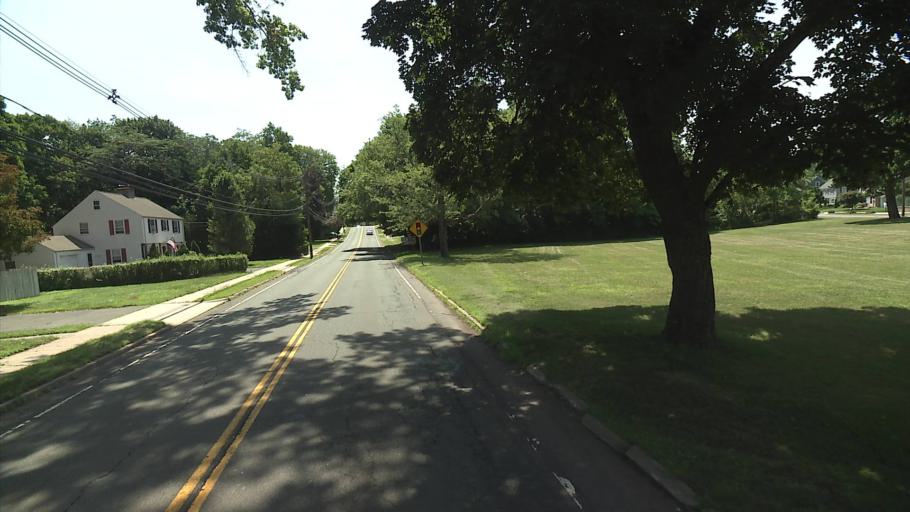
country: US
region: Connecticut
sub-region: Hartford County
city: New Britain
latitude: 41.6549
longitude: -72.7972
